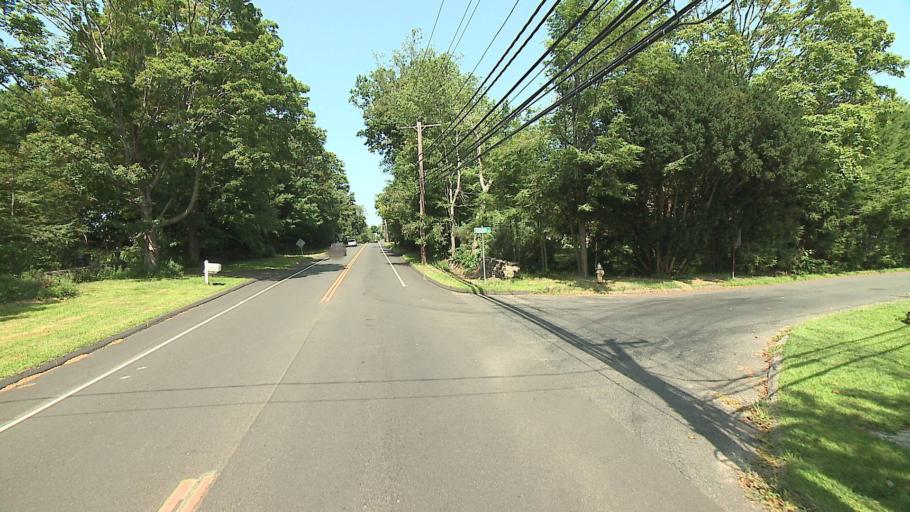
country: US
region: Connecticut
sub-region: Fairfield County
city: Trumbull
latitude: 41.2304
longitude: -73.2624
